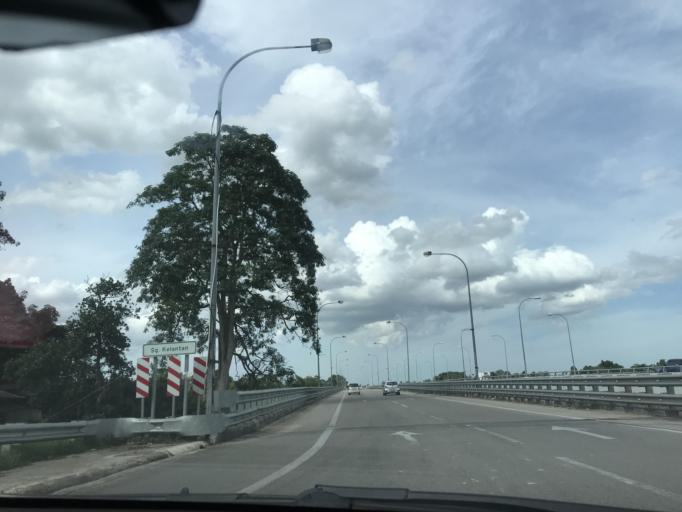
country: MY
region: Kelantan
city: Kampung Lemal
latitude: 6.0301
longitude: 102.1425
